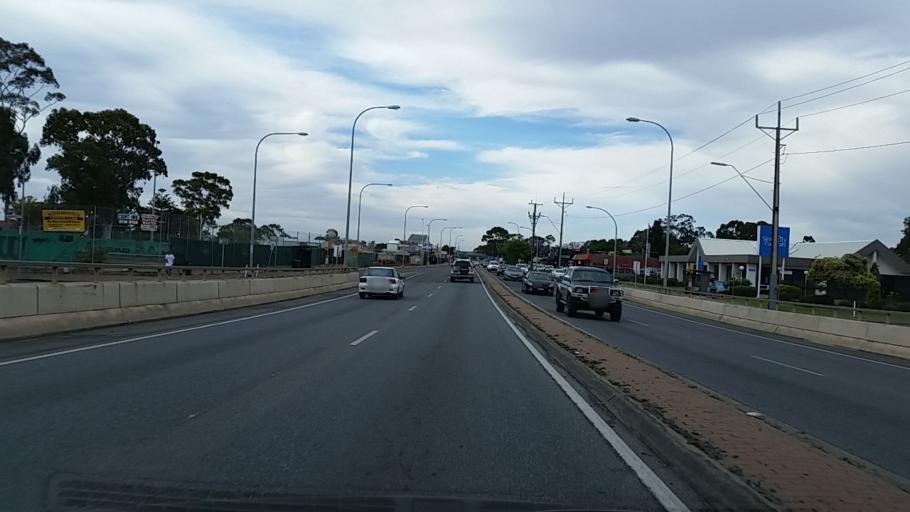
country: AU
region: South Australia
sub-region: Mitcham
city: Clarence Gardens
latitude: -34.9654
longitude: 138.5728
